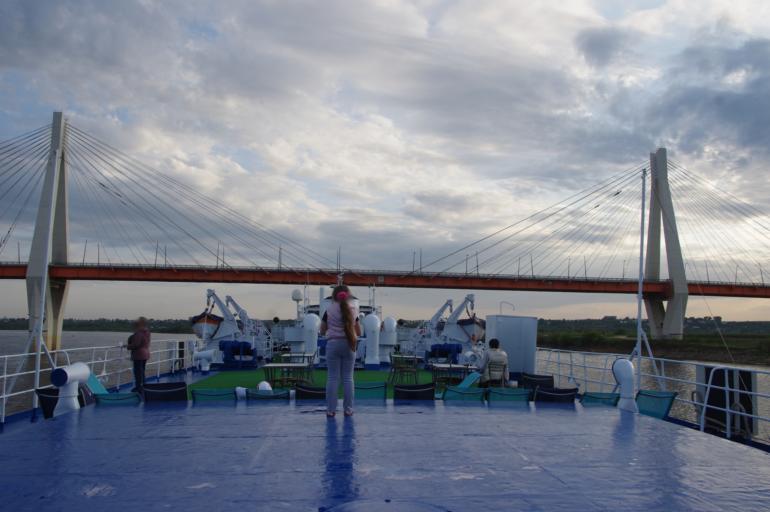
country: RU
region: Vladimir
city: Murom
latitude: 55.6198
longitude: 42.0697
